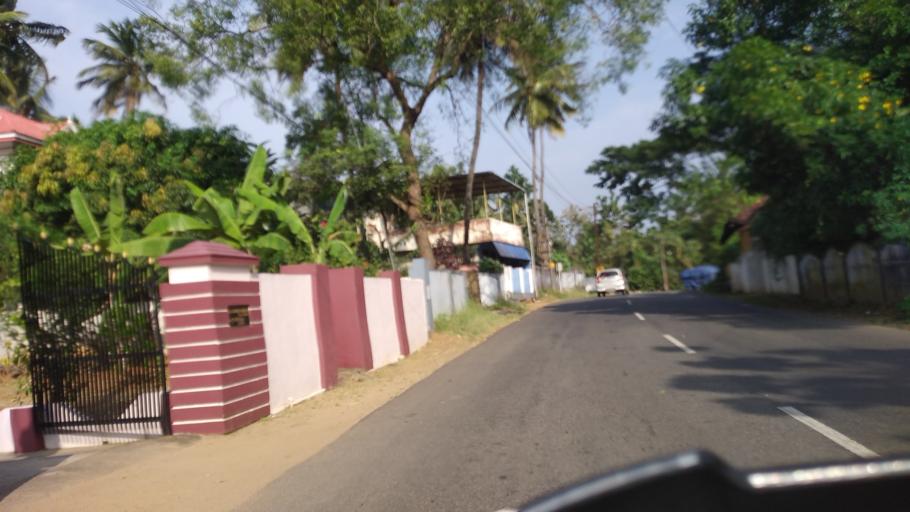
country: IN
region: Kerala
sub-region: Palakkad district
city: Palakkad
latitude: 10.6017
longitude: 76.5464
